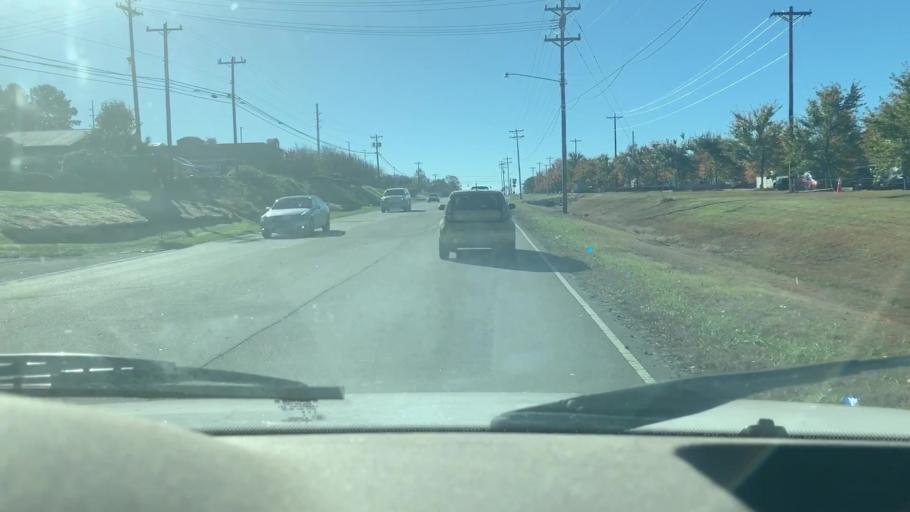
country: US
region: North Carolina
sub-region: Mecklenburg County
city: Huntersville
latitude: 35.4132
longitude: -80.8560
